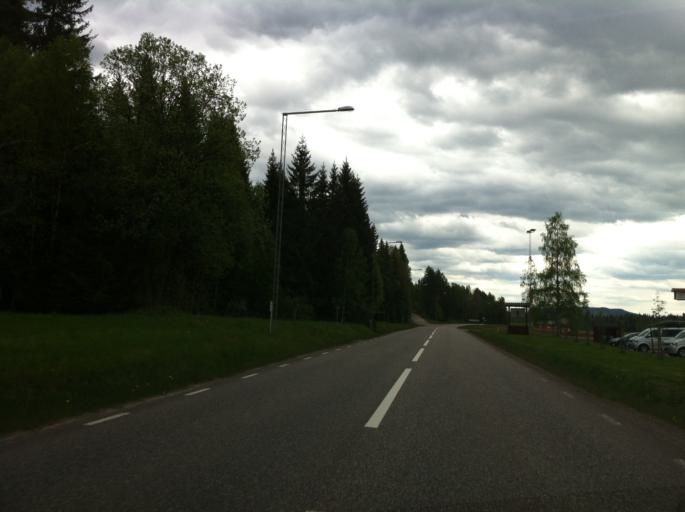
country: SE
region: Dalarna
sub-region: Malung-Saelens kommun
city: Malung
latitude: 61.1143
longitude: 13.2930
